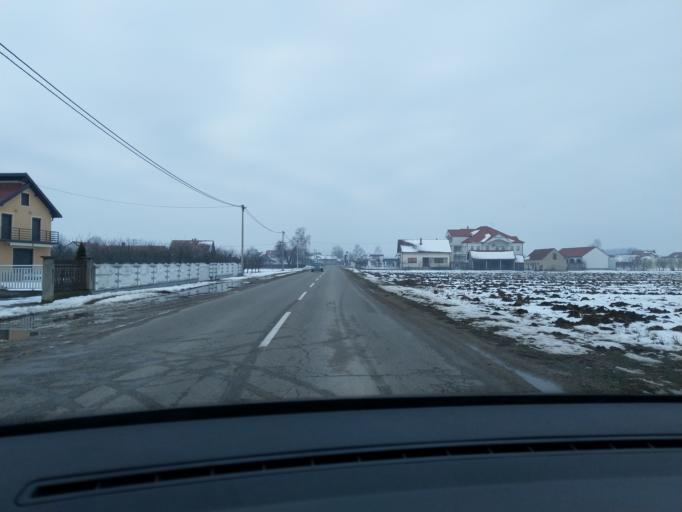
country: BA
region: Republika Srpska
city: Velika Obarska
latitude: 44.7907
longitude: 19.1809
